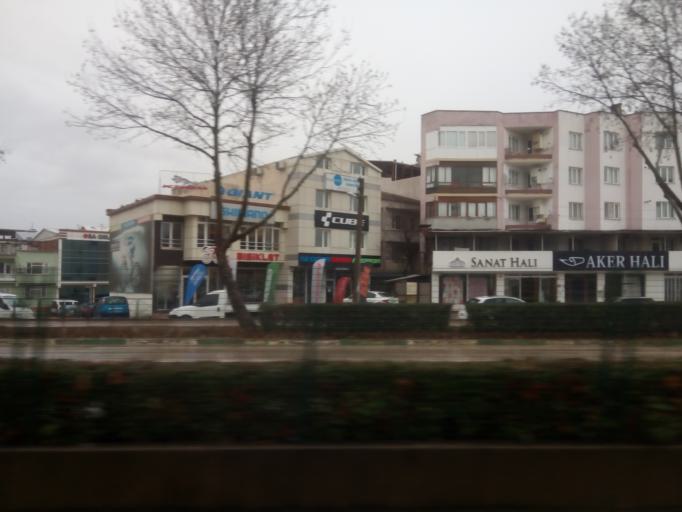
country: TR
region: Bursa
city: Yildirim
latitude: 40.2245
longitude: 28.9924
